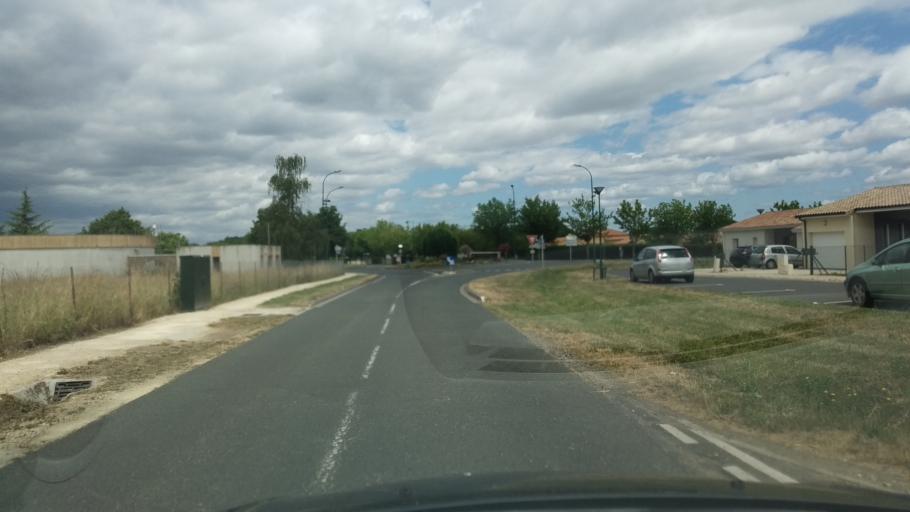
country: FR
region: Poitou-Charentes
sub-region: Departement de la Vienne
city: Vouneuil-sous-Biard
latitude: 46.5676
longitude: 0.2715
